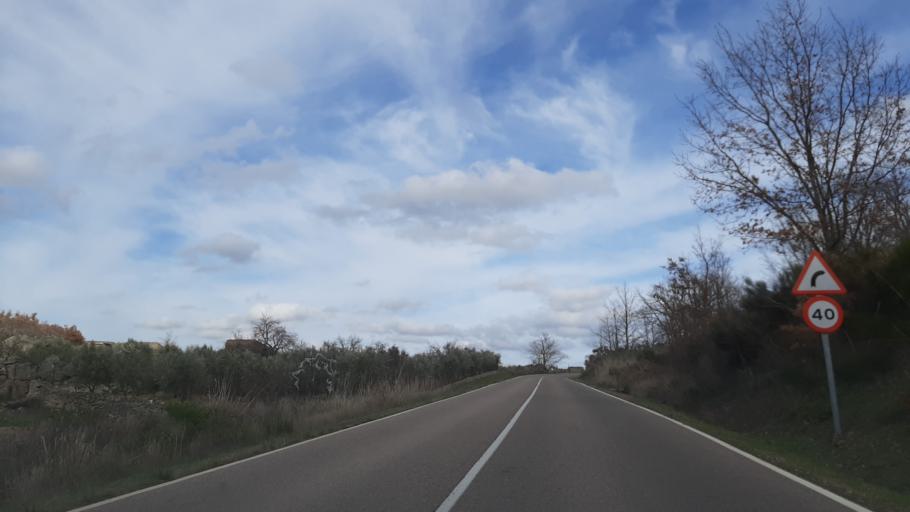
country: ES
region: Castille and Leon
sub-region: Provincia de Salamanca
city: Villarino de los Aires
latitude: 41.2625
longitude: -6.4287
